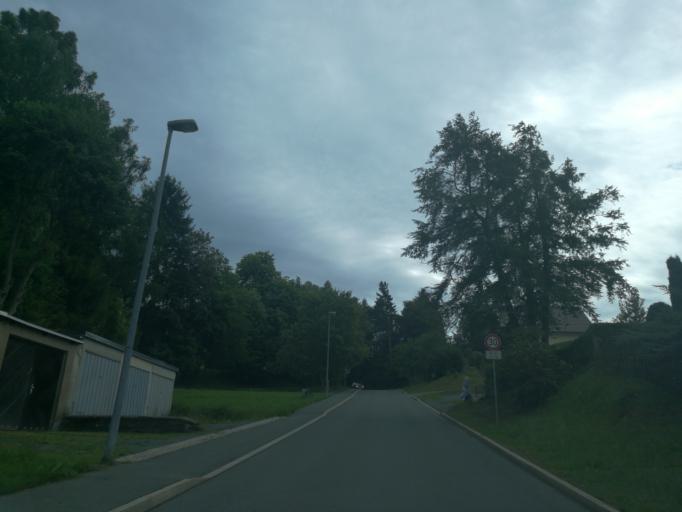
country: DE
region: Saxony
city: Adorf
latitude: 50.3171
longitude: 12.2614
